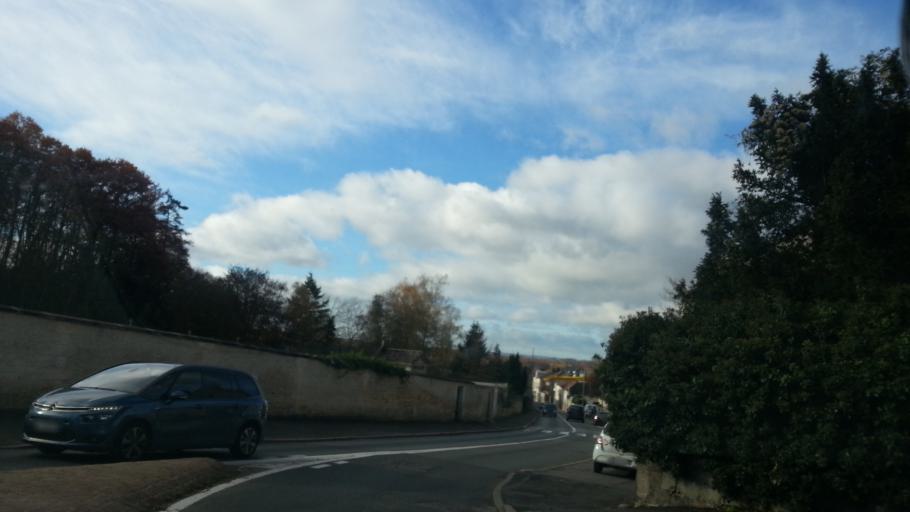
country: FR
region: Picardie
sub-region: Departement de l'Oise
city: Gouvieux
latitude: 49.1883
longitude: 2.4272
